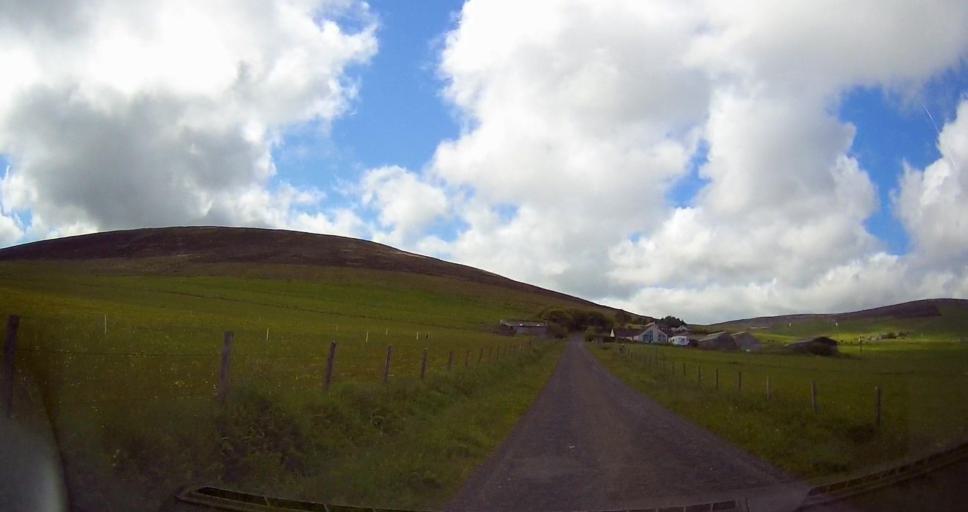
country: GB
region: Scotland
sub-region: Orkney Islands
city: Orkney
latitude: 59.0479
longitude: -3.0950
